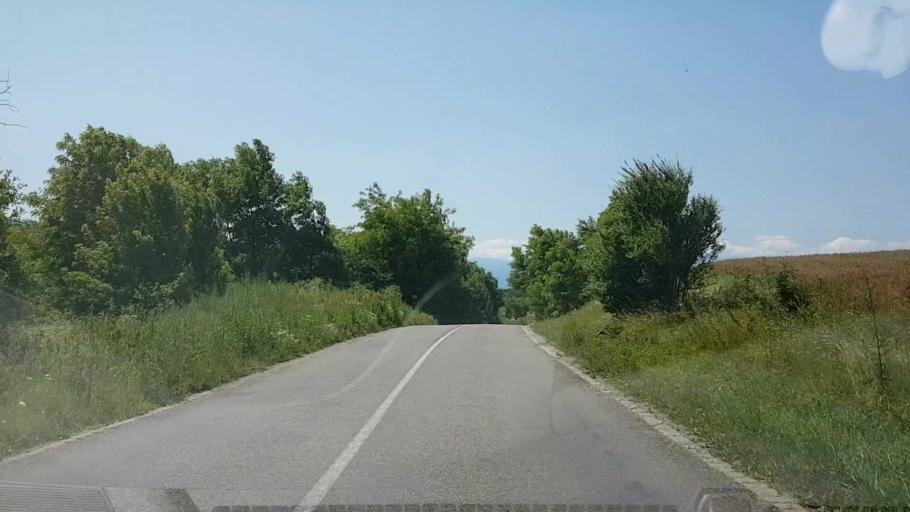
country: RO
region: Brasov
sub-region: Comuna Cincu
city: Cincu
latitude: 45.8982
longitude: 24.8121
